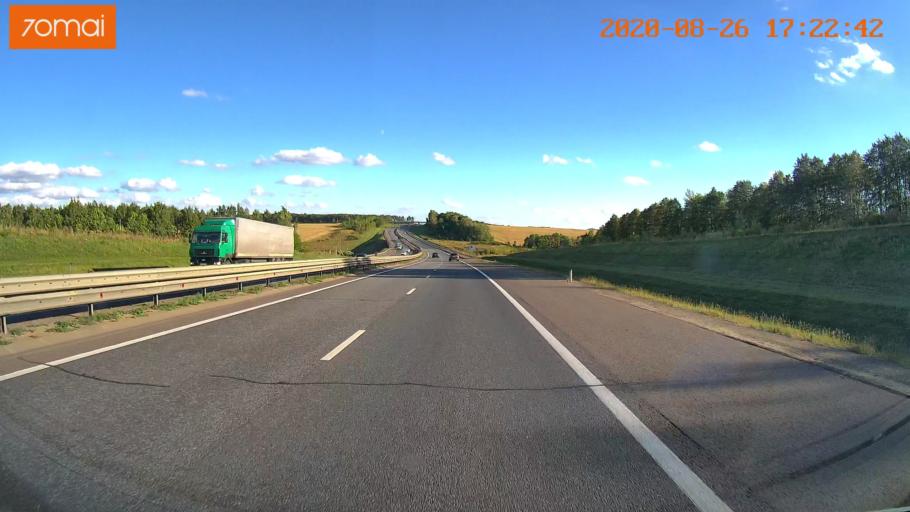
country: RU
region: Tula
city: Volovo
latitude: 53.5460
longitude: 38.1136
